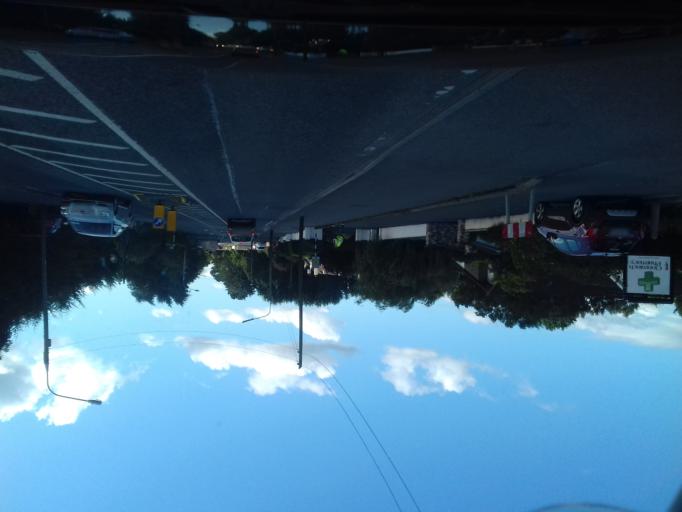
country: IE
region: Leinster
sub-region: Uibh Fhaili
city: Tullamore
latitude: 53.2632
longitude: -7.4852
